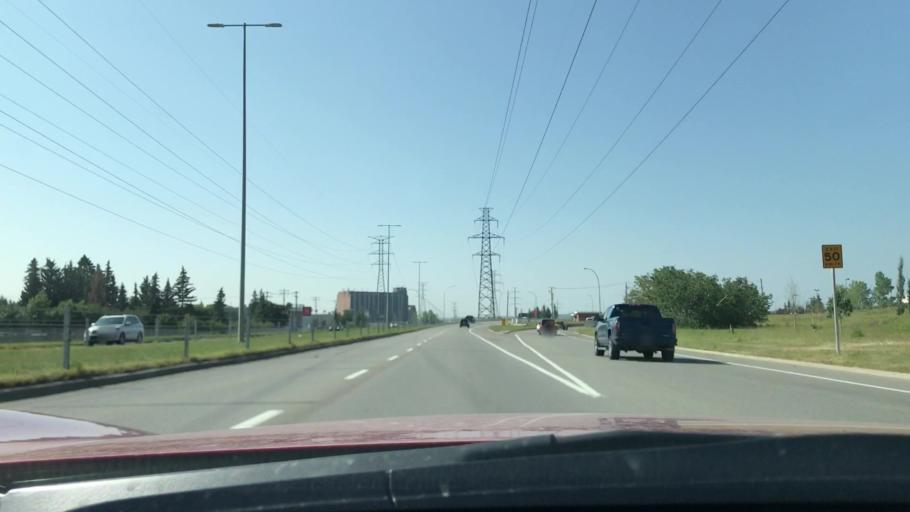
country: CA
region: Alberta
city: Calgary
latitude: 51.0245
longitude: -114.1644
